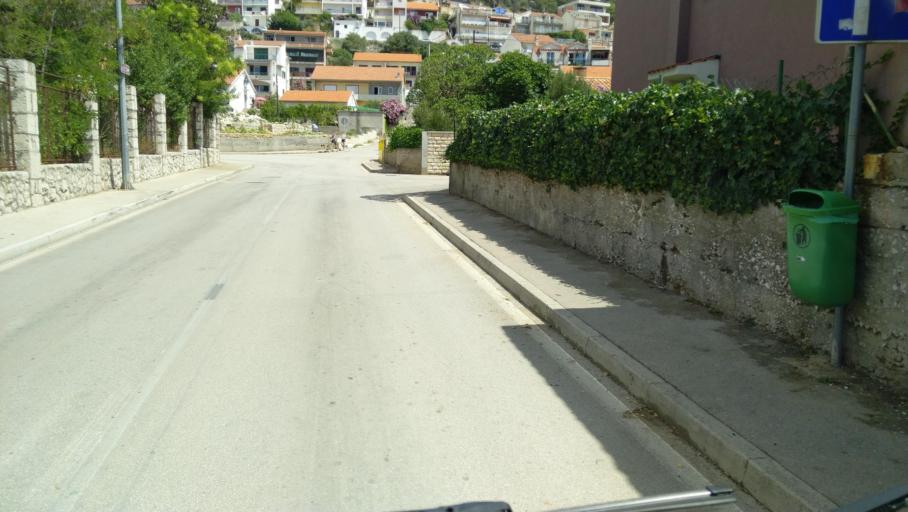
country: HR
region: Sibensko-Kniniska
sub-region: Grad Sibenik
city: Sibenik
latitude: 43.7434
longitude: 15.8867
